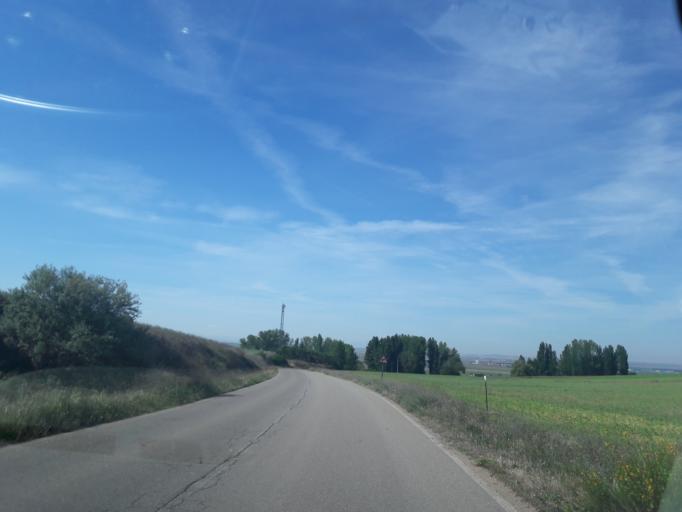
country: ES
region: Castille and Leon
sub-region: Provincia de Salamanca
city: Villoruela
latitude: 41.0160
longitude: -5.3945
